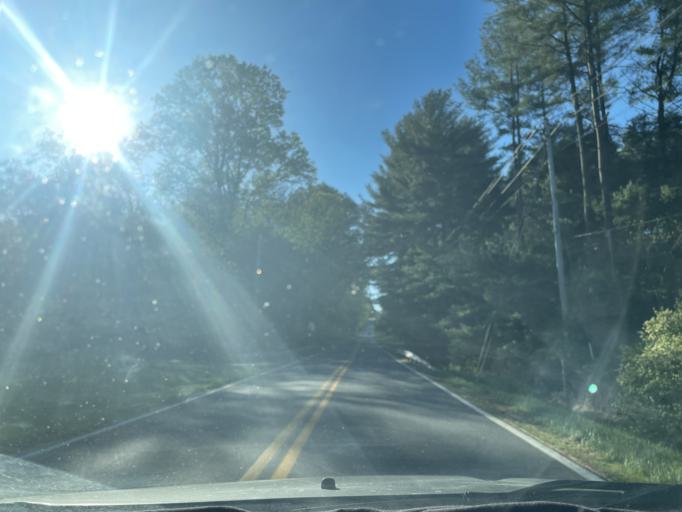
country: US
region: Maryland
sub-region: Carroll County
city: Mount Airy
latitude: 39.4120
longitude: -77.1360
